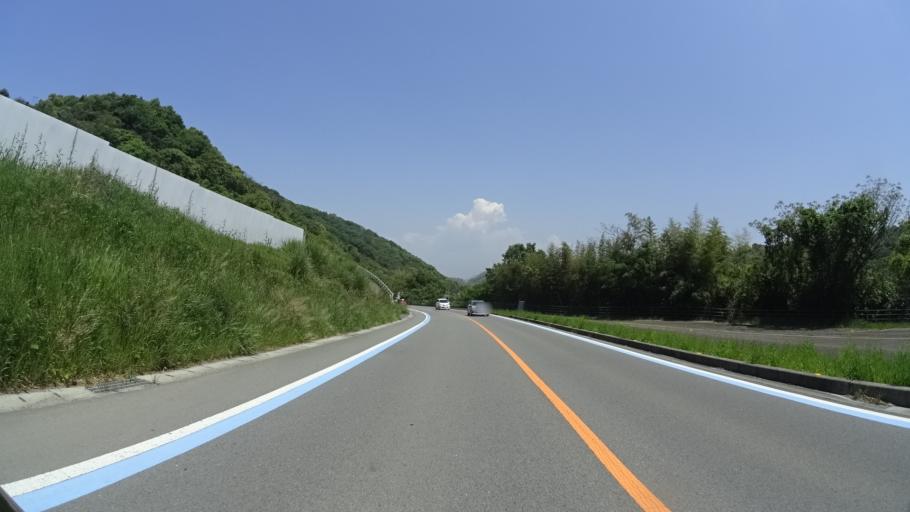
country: JP
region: Ehime
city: Iyo
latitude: 33.7249
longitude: 132.6831
